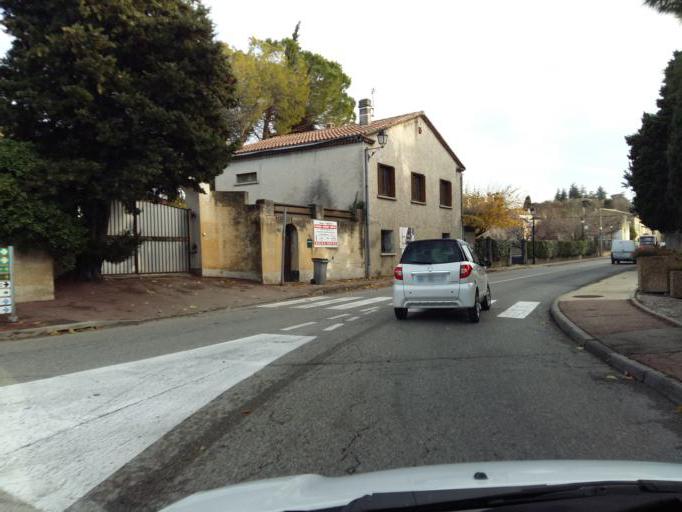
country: FR
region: Provence-Alpes-Cote d'Azur
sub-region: Departement du Vaucluse
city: Visan
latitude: 44.3185
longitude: 4.9486
